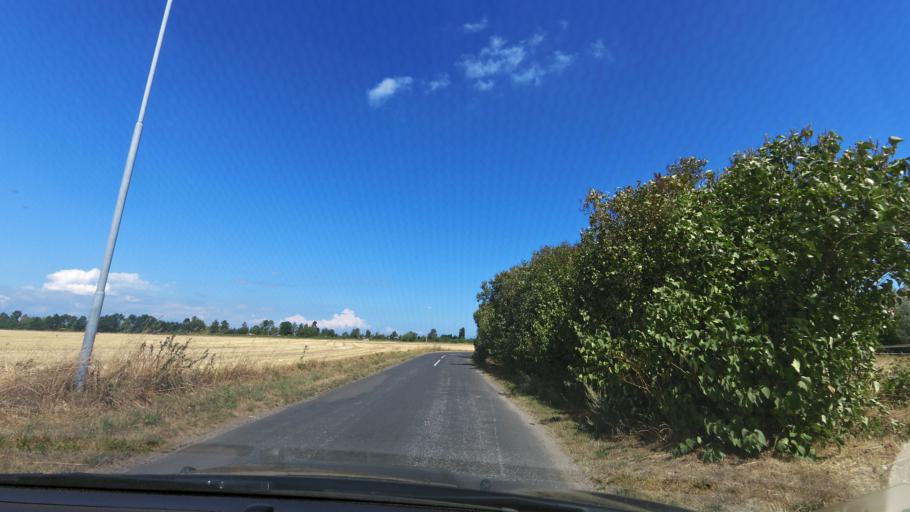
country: DK
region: South Denmark
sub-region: Nordfyns Kommune
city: Otterup
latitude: 55.5515
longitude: 10.4697
